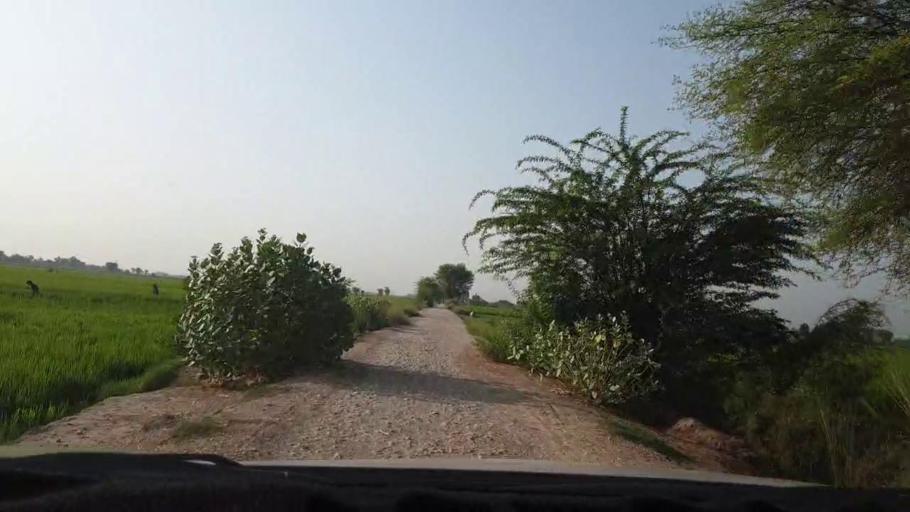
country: PK
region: Sindh
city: Larkana
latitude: 27.5082
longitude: 68.1729
